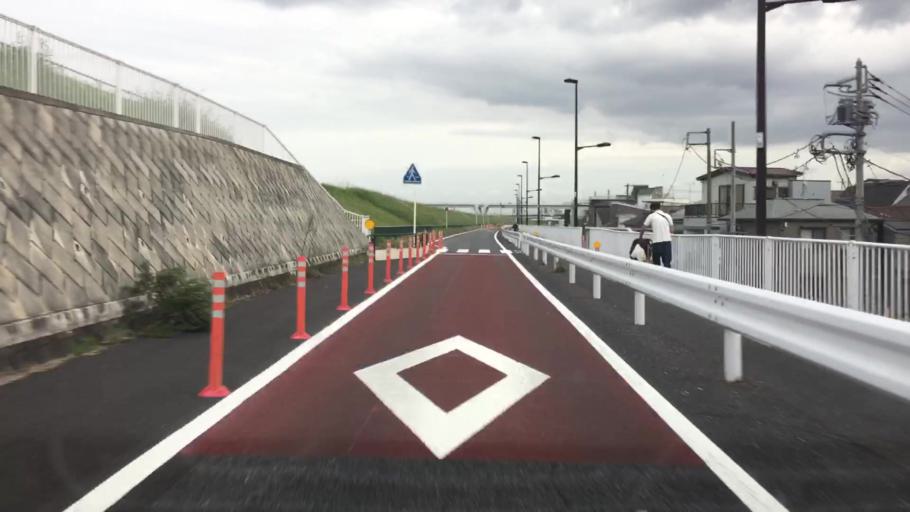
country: JP
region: Saitama
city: Soka
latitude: 35.7497
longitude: 139.8135
